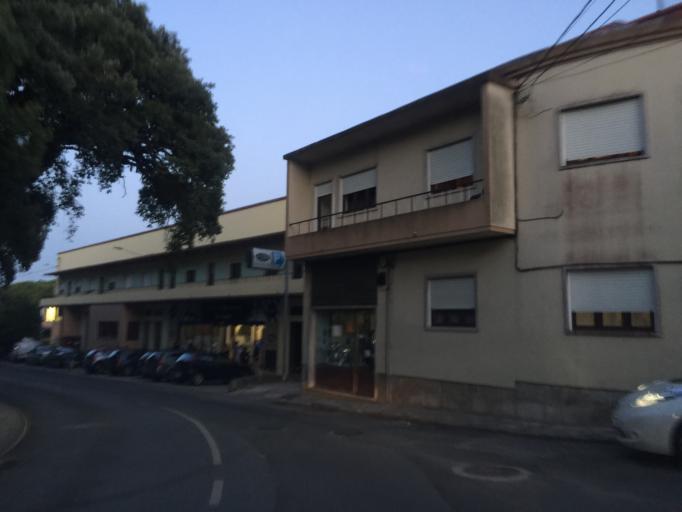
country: PT
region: Leiria
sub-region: Bombarral
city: Bombarral
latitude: 39.2665
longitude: -9.1580
